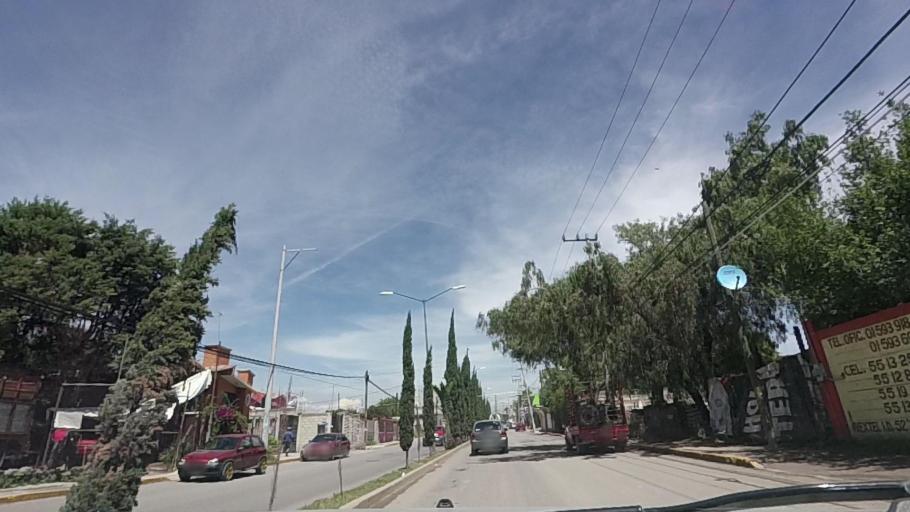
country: MX
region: Mexico
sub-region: Huehuetoca
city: Casa Nueva
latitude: 19.8306
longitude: -99.2209
